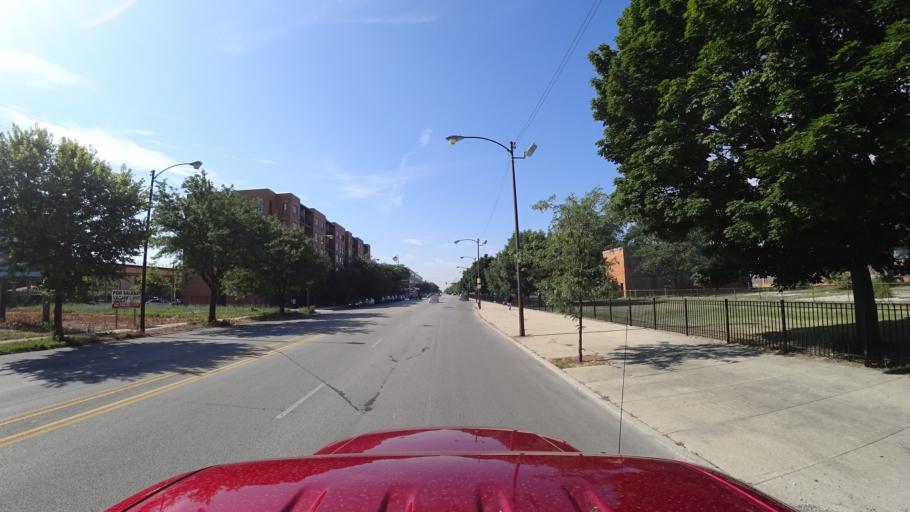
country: US
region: Illinois
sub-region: Cook County
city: Chicago
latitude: 41.8251
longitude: -87.6265
